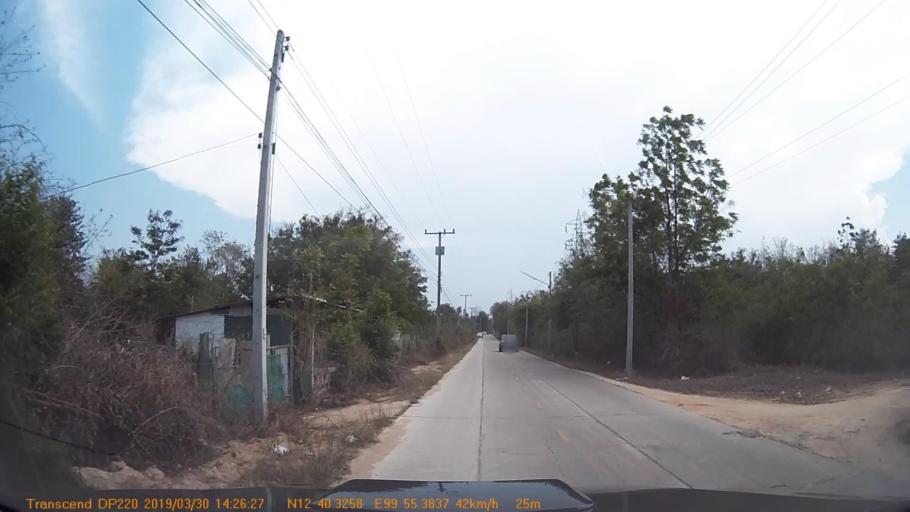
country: TH
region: Prachuap Khiri Khan
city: Hua Hin
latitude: 12.6719
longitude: 99.9231
